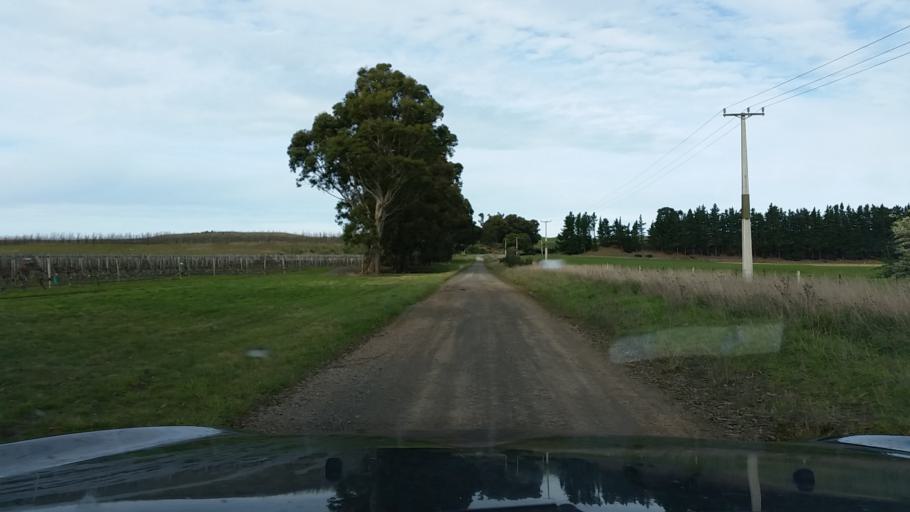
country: NZ
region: Marlborough
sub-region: Marlborough District
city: Blenheim
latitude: -41.6353
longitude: 174.1201
